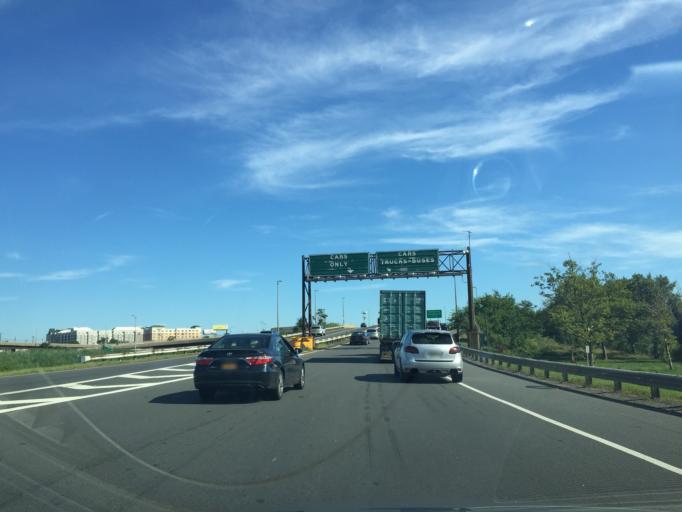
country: US
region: New Jersey
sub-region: Union County
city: Elizabeth
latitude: 40.6674
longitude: -74.1837
